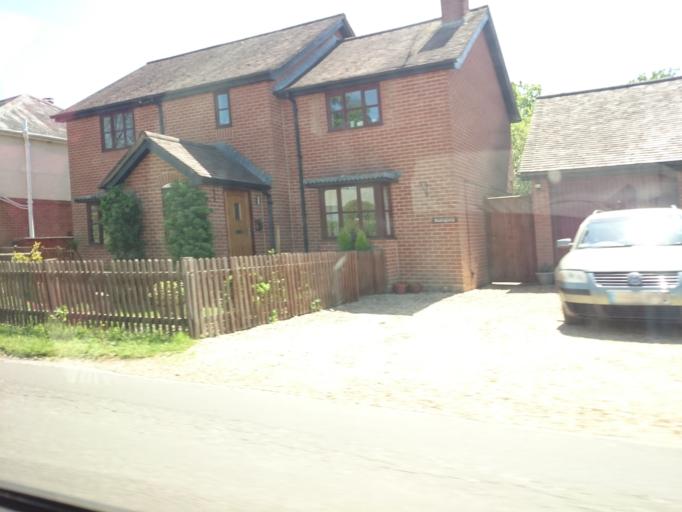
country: GB
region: England
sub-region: Hampshire
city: Cadnam
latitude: 50.9143
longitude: -1.5642
